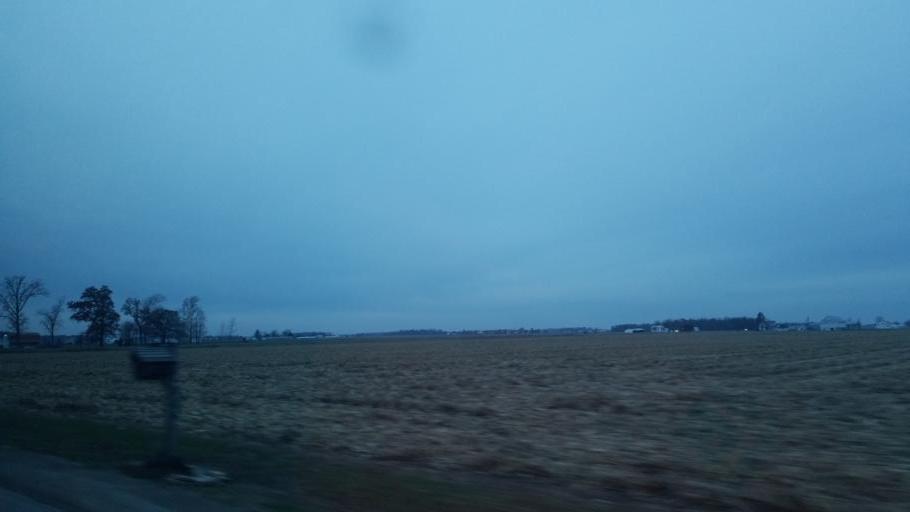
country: US
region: Indiana
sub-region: Adams County
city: Berne
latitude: 40.7309
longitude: -84.9530
